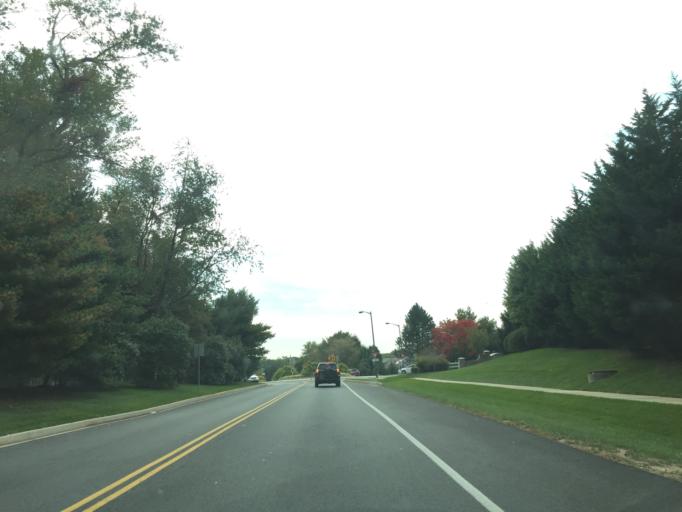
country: US
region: Maryland
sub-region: Harford County
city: Bel Air South
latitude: 39.4791
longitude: -76.3274
